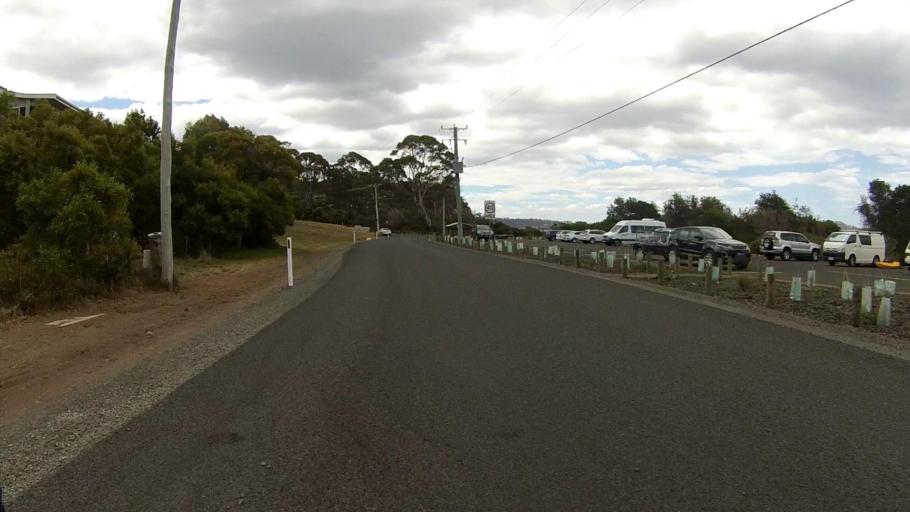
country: AU
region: Tasmania
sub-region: Sorell
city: Sorell
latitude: -42.5801
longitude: 147.9094
